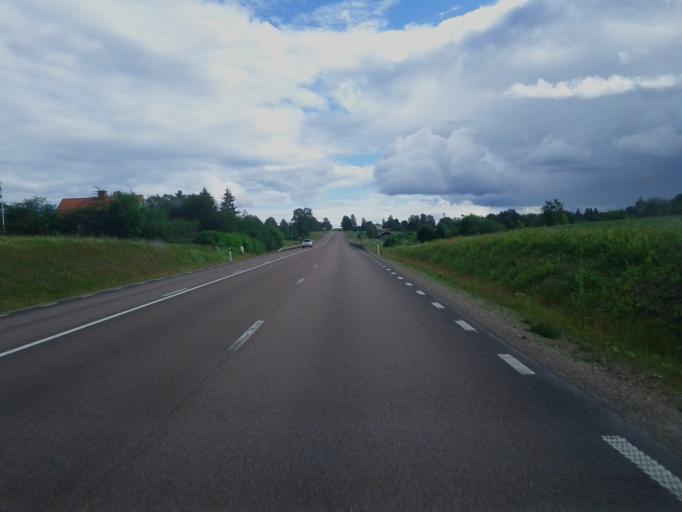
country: SE
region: Dalarna
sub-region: Rattviks Kommun
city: Raettvik
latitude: 60.8497
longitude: 15.1147
